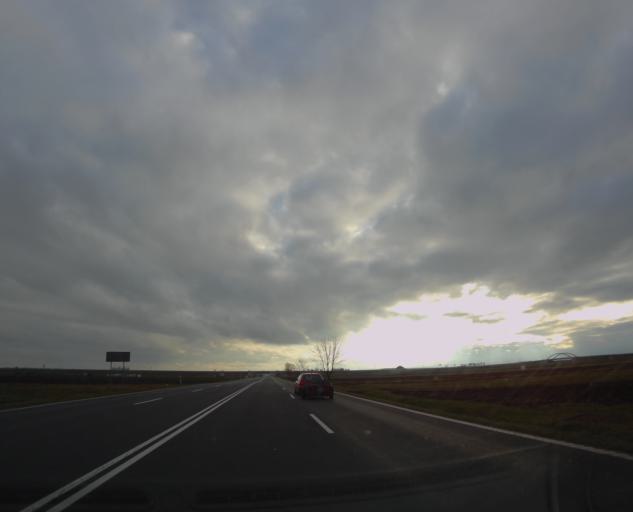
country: PL
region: Subcarpathian Voivodeship
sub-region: Powiat jaroslawski
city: Radymno
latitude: 49.9168
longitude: 22.8201
